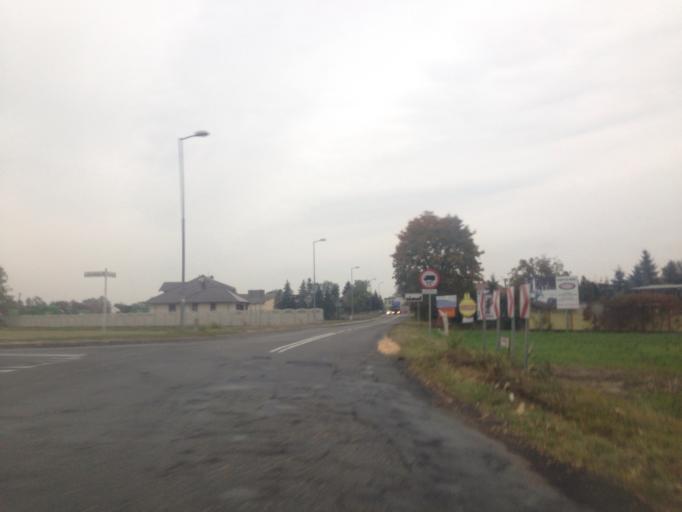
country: PL
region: Greater Poland Voivodeship
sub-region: Powiat poznanski
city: Kleszczewo
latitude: 52.3599
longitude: 17.1331
